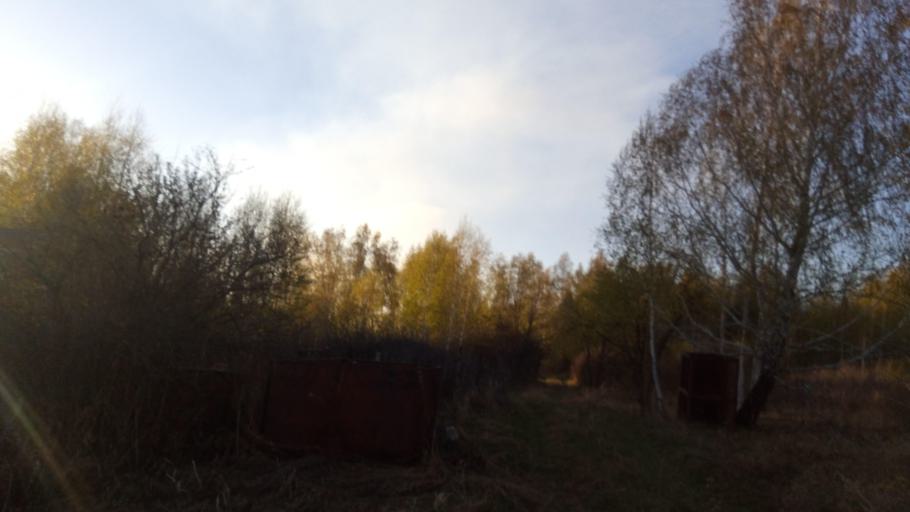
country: RU
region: Chelyabinsk
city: Timiryazevskiy
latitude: 54.9930
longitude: 60.8562
